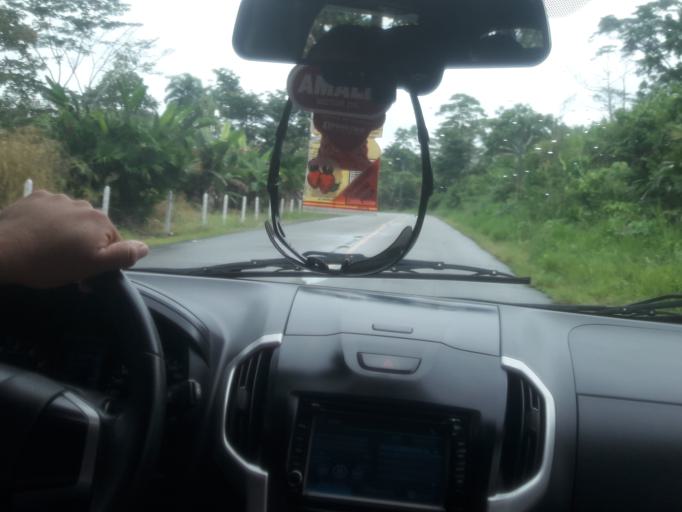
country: EC
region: Napo
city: Tena
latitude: -1.0355
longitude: -77.6896
